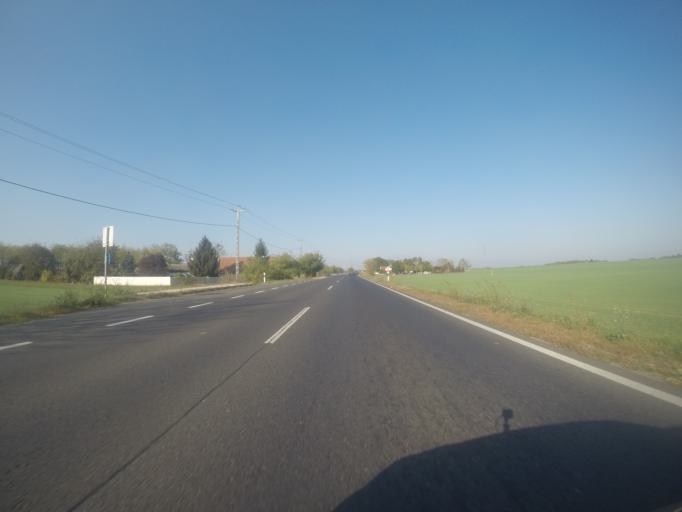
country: HU
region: Tolna
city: Dunafoldvar
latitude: 46.8408
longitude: 18.9101
